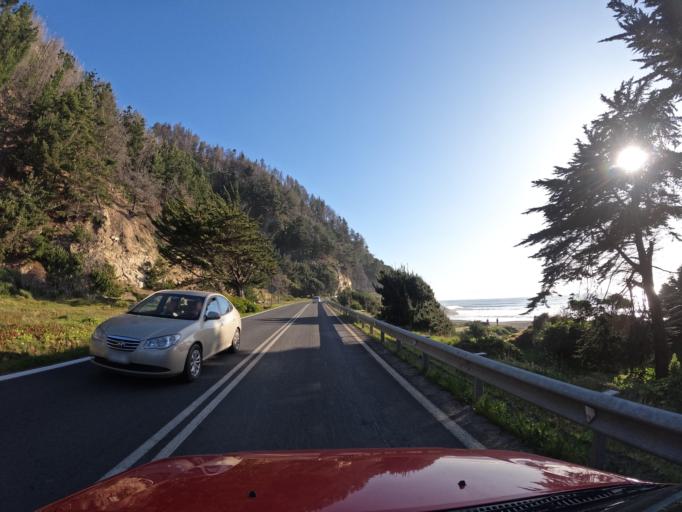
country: CL
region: Maule
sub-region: Provincia de Talca
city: Constitucion
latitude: -35.3484
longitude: -72.4381
